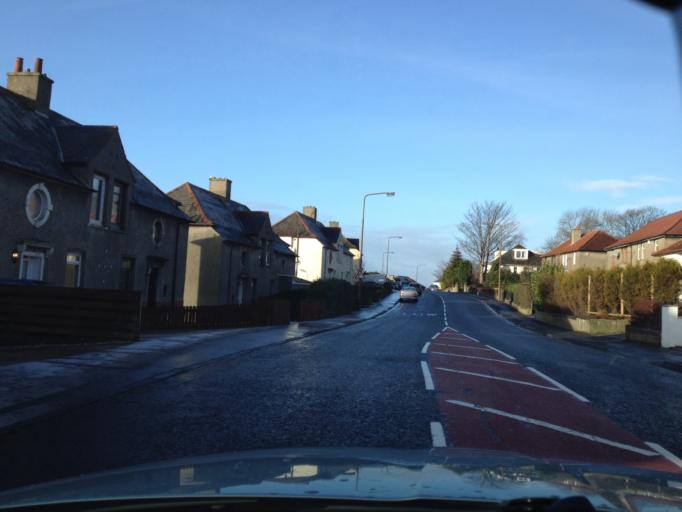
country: GB
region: Scotland
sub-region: West Lothian
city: Bathgate
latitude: 55.8973
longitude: -3.6295
